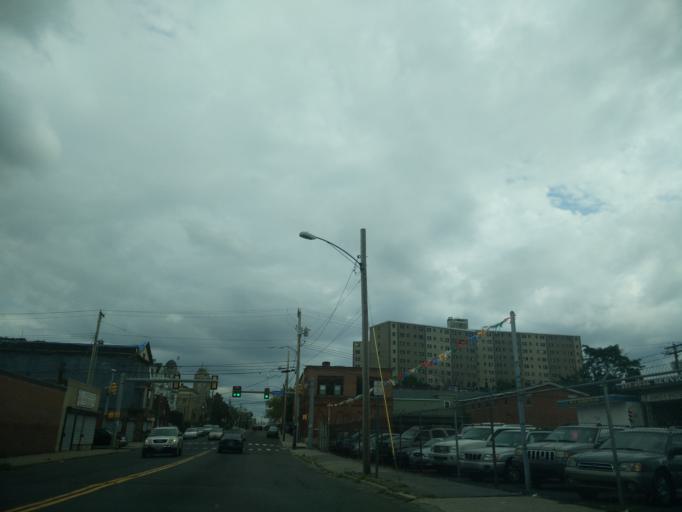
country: US
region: Connecticut
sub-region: Fairfield County
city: Bridgeport
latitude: 41.1860
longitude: -73.1883
